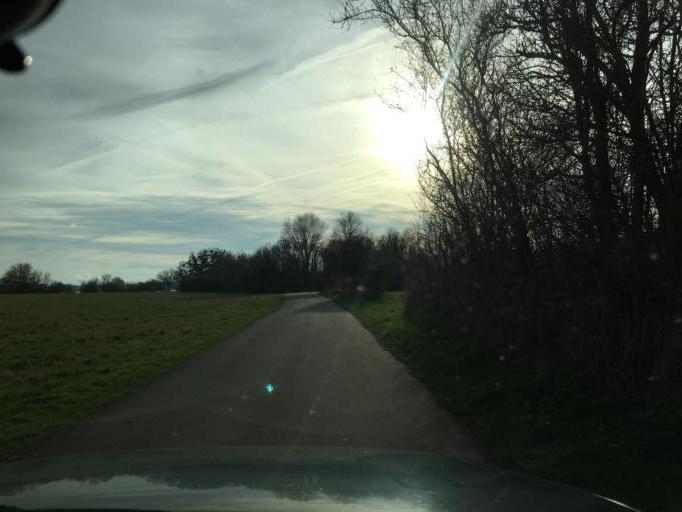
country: FR
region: Centre
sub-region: Departement du Loiret
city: Beaugency
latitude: 47.7881
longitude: 1.6522
